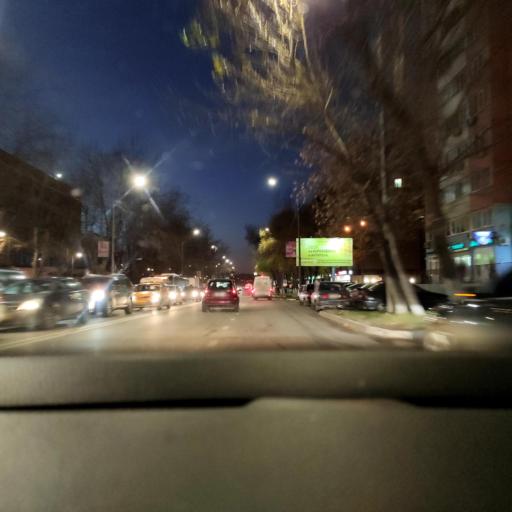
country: RU
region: Moskovskaya
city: Reutov
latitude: 55.7667
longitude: 37.8490
